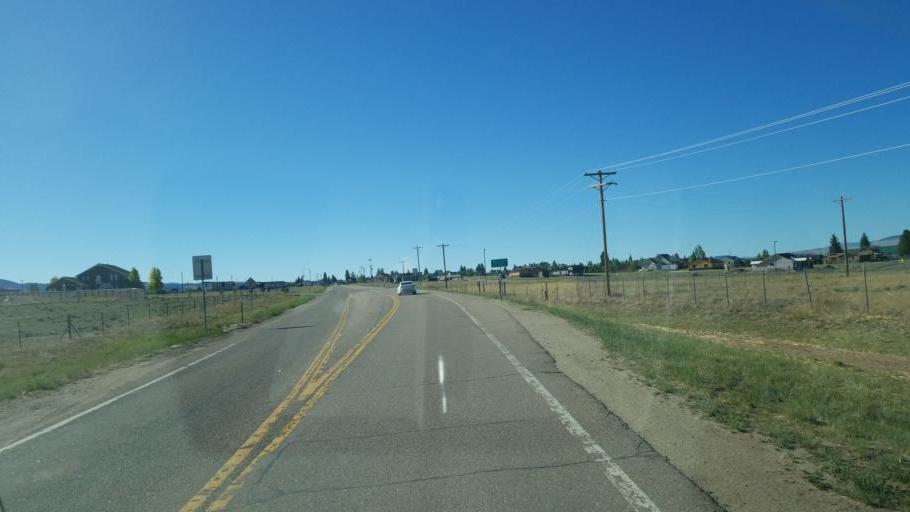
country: US
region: Colorado
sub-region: Custer County
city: Westcliffe
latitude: 38.1427
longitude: -105.4734
